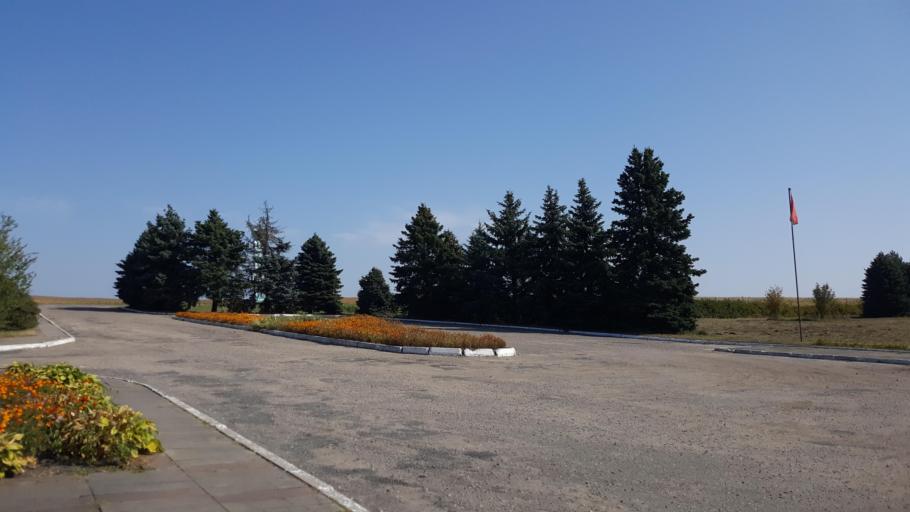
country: BY
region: Brest
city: Kamyanyets
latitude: 52.4169
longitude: 23.6872
